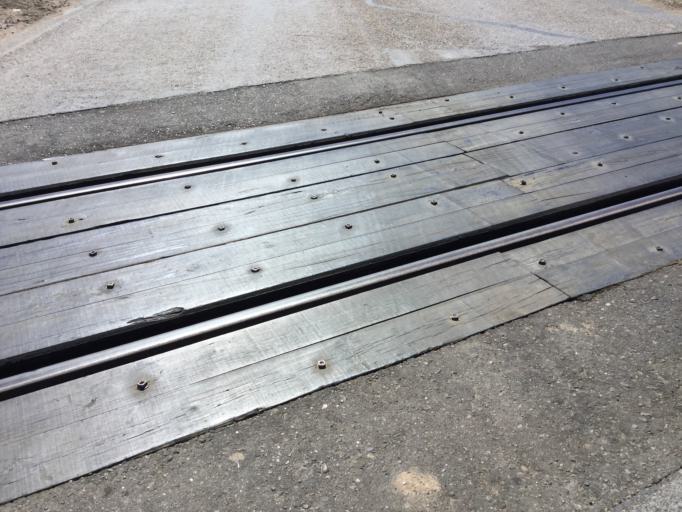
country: US
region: Kansas
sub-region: Grant County
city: Ulysses
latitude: 37.5823
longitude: -101.3452
